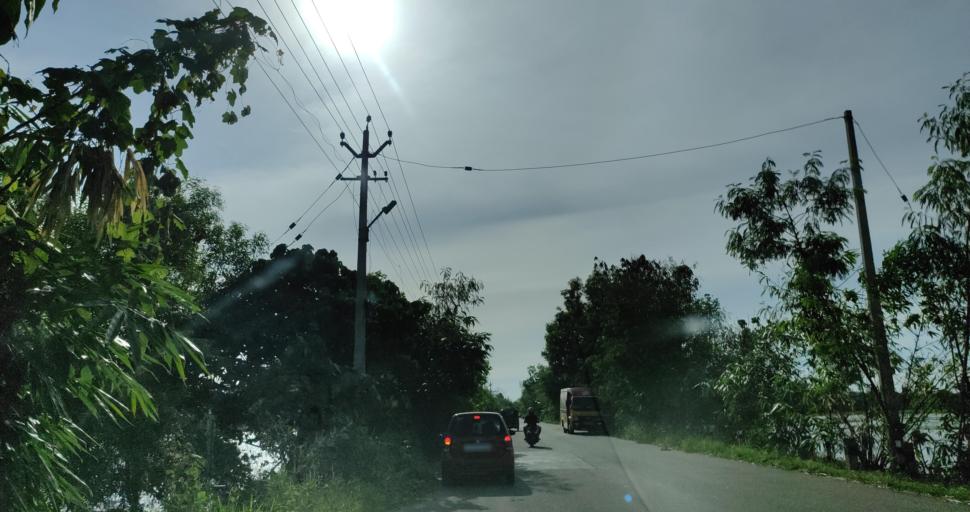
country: IN
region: Kerala
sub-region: Kottayam
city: Kottayam
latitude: 9.5648
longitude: 76.5082
